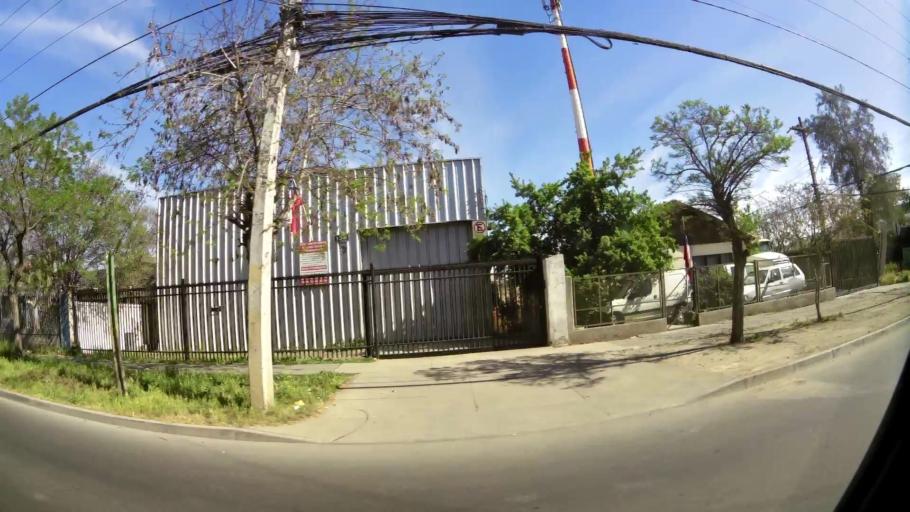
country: CL
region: Santiago Metropolitan
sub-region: Provincia de Santiago
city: Lo Prado
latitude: -33.4924
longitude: -70.7061
